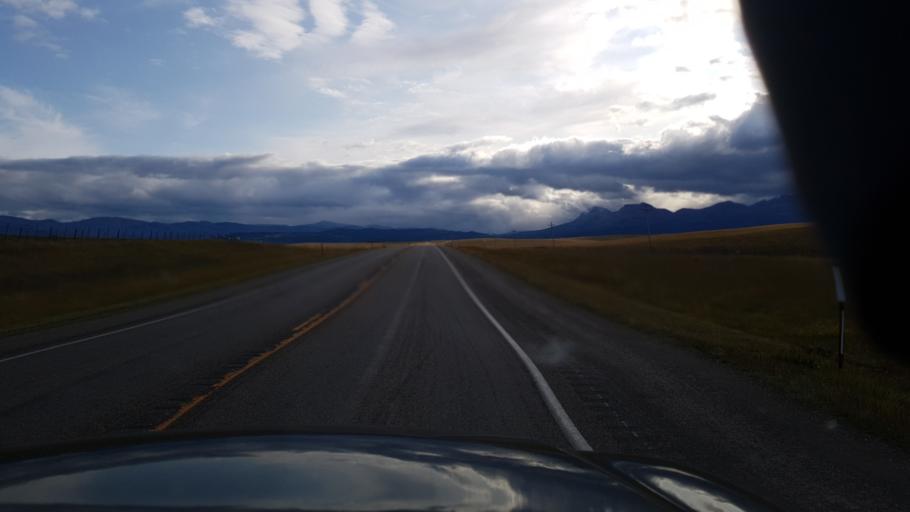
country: US
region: Montana
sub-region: Glacier County
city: South Browning
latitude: 48.4828
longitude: -113.1365
